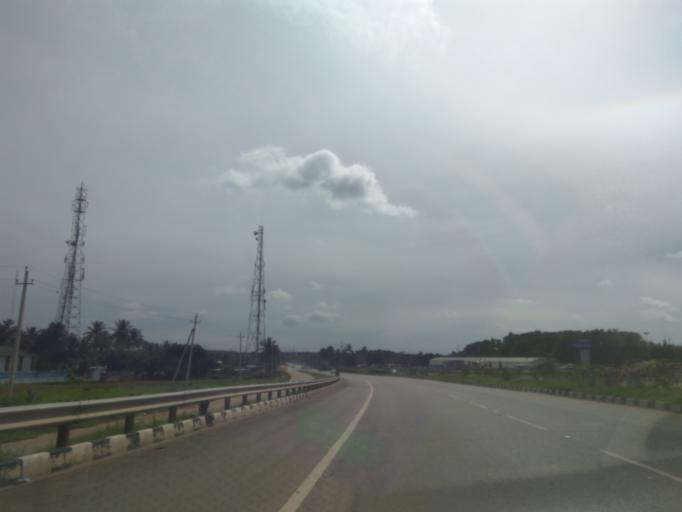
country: IN
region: Karnataka
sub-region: Bangalore Rural
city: Dasarahalli
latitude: 13.1279
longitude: 77.9137
